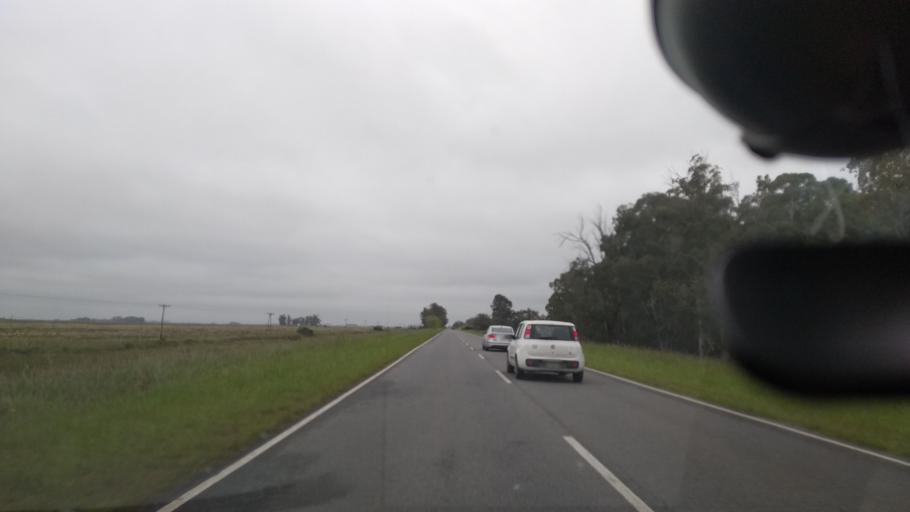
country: AR
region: Buenos Aires
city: Veronica
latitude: -35.4634
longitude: -57.3269
